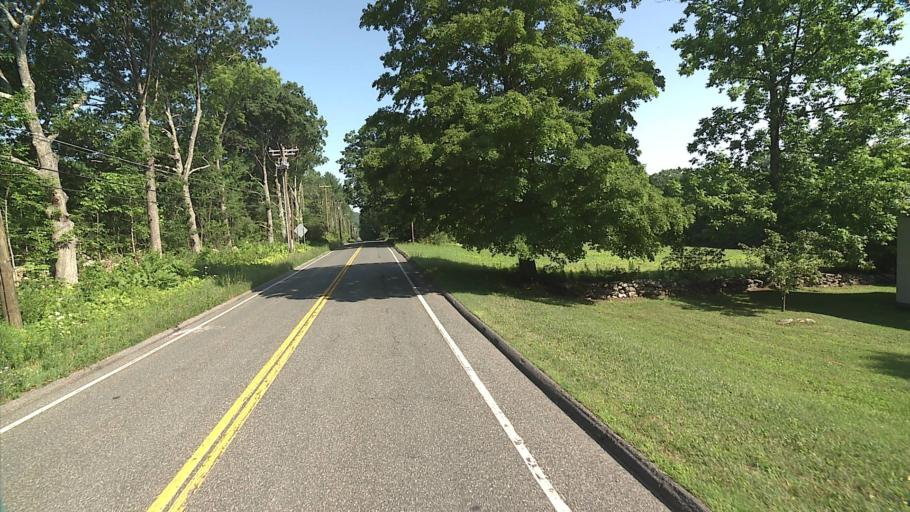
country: US
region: Connecticut
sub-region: Litchfield County
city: Winsted
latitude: 42.0073
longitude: -73.1075
